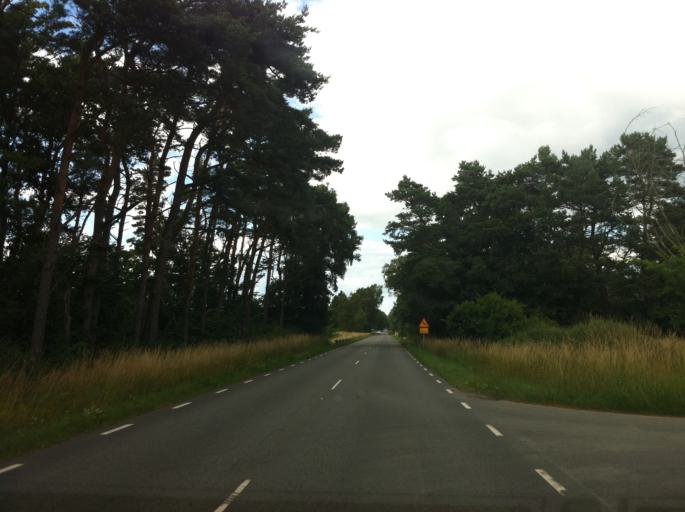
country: SE
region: Skane
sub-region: Simrishamns Kommun
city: Simrishamn
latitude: 55.4079
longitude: 14.1897
